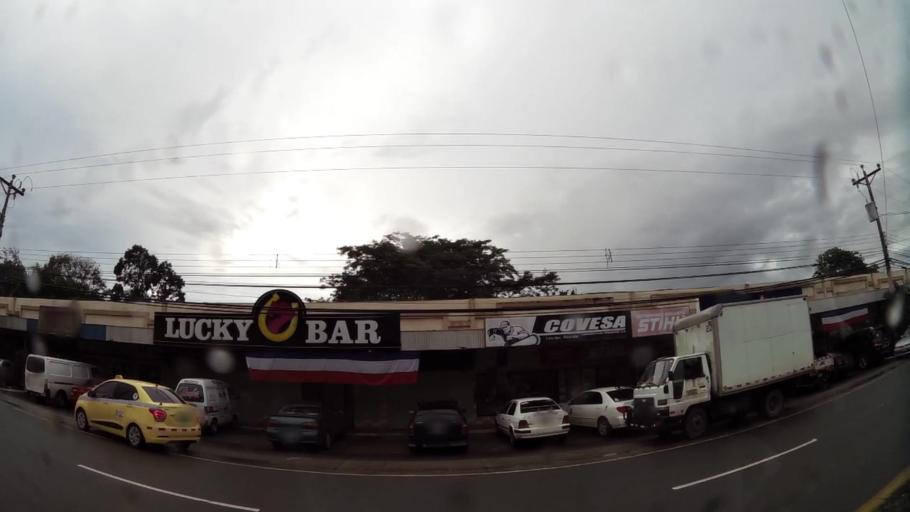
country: PA
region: Veraguas
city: Santiago de Veraguas
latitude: 8.1029
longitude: -80.9744
